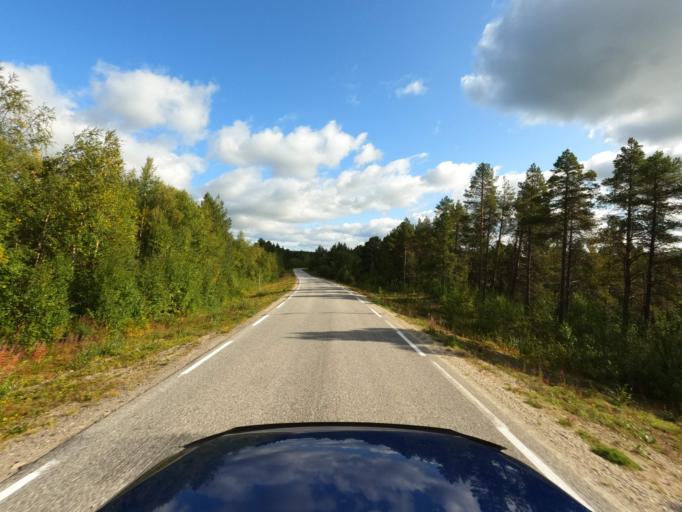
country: NO
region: Finnmark Fylke
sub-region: Karasjok
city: Karasjohka
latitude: 69.4317
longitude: 25.1320
